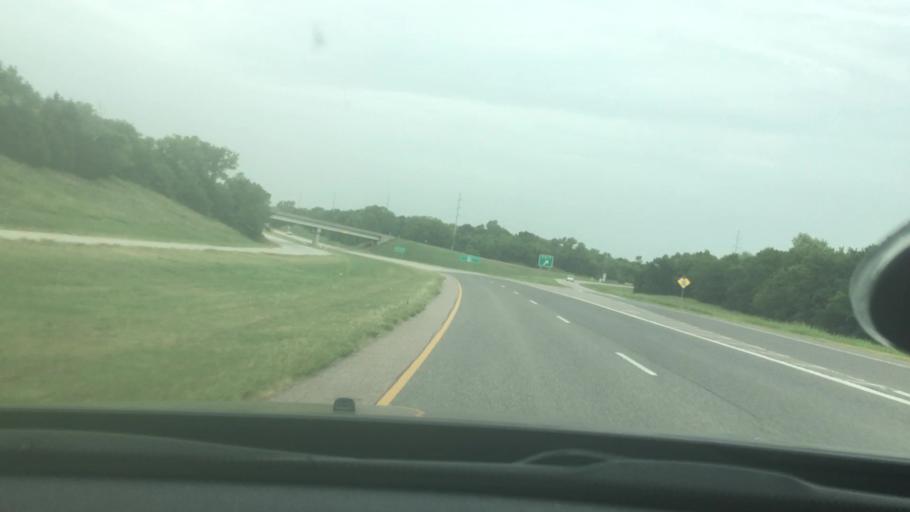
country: US
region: Oklahoma
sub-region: Pontotoc County
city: Ada
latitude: 34.7481
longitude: -96.6541
